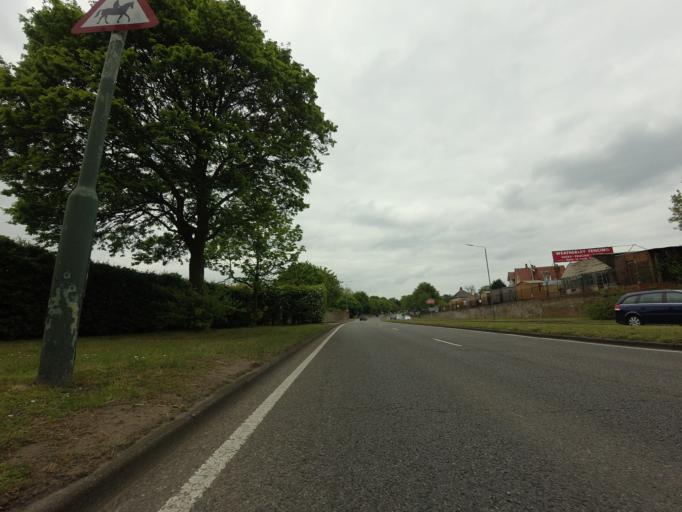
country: GB
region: England
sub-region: Greater London
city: Bexley
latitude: 51.4241
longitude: 0.1342
